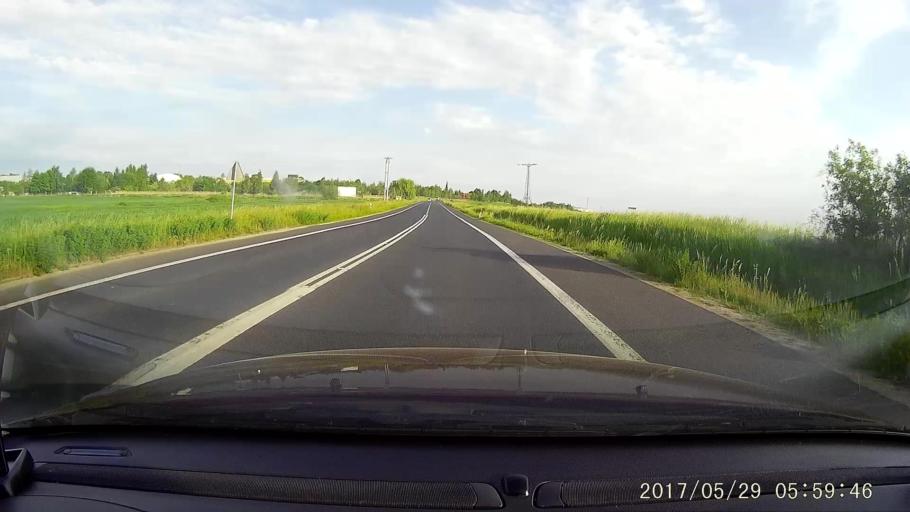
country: PL
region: Lower Silesian Voivodeship
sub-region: Powiat zgorzelecki
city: Lagow
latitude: 51.1460
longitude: 15.0338
